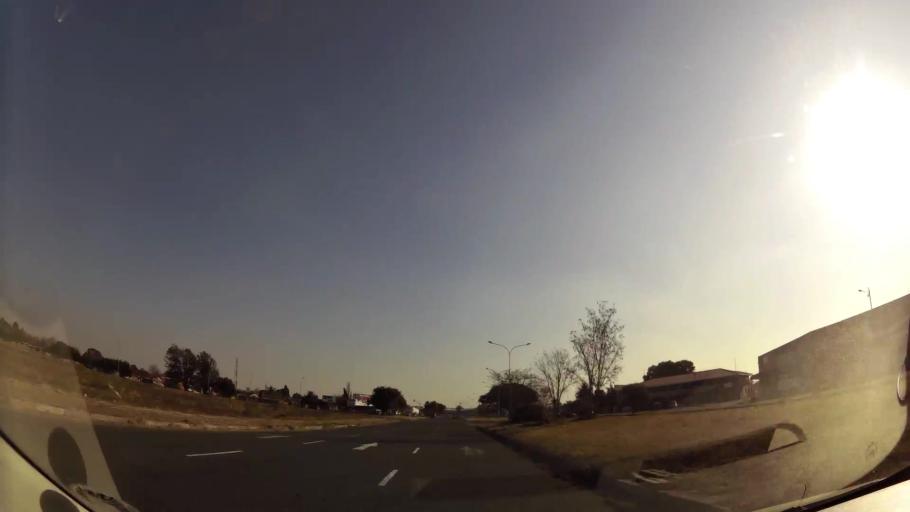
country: ZA
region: Gauteng
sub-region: West Rand District Municipality
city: Randfontein
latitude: -26.1738
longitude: 27.7085
